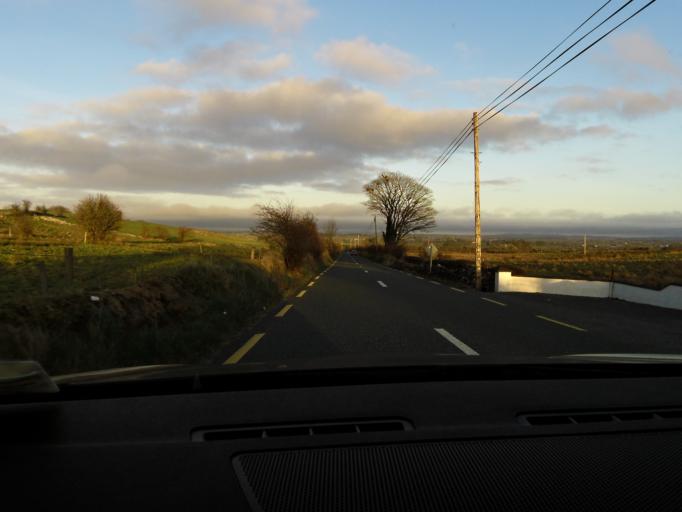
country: IE
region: Connaught
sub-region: Sligo
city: Tobercurry
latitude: 54.0450
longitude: -8.6757
